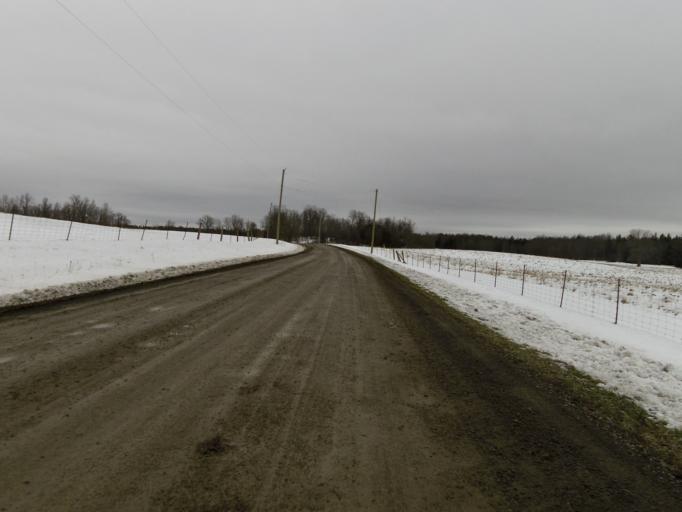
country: CA
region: Ontario
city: Carleton Place
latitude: 45.2021
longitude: -76.2134
